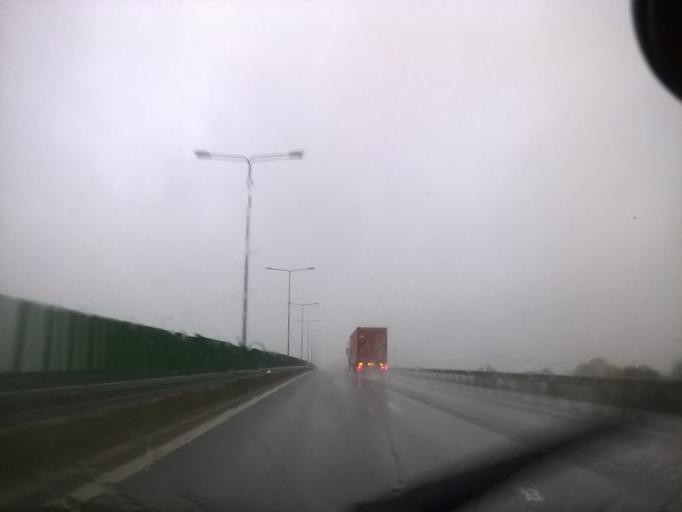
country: PL
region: Warmian-Masurian Voivodeship
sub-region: Powiat elblaski
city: Elblag
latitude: 54.1431
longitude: 19.3948
